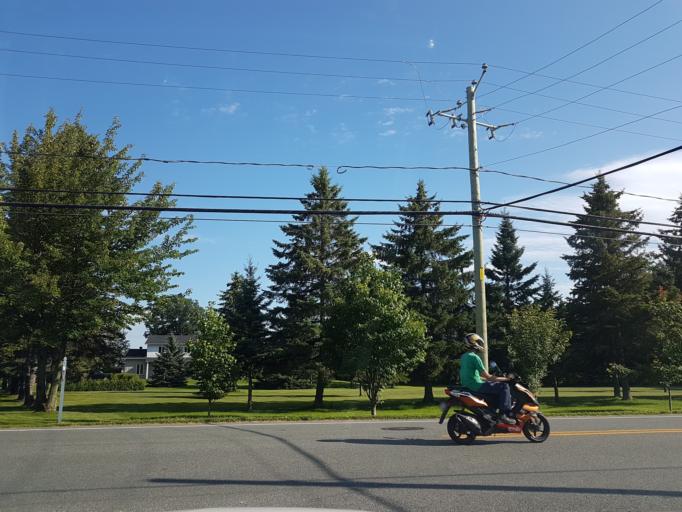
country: CA
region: Quebec
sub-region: Mauricie
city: Nicolet
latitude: 46.2881
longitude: -72.6418
